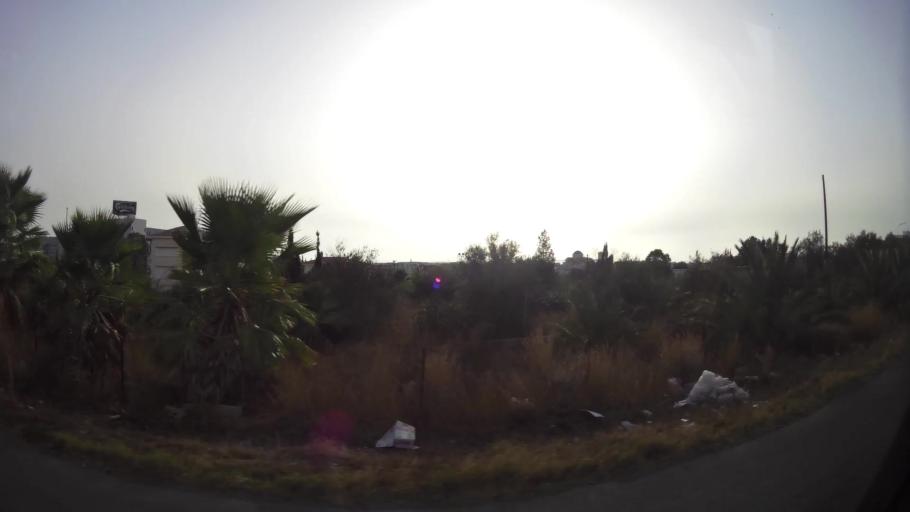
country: CY
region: Lefkosia
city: Geri
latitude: 35.0732
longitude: 33.3808
